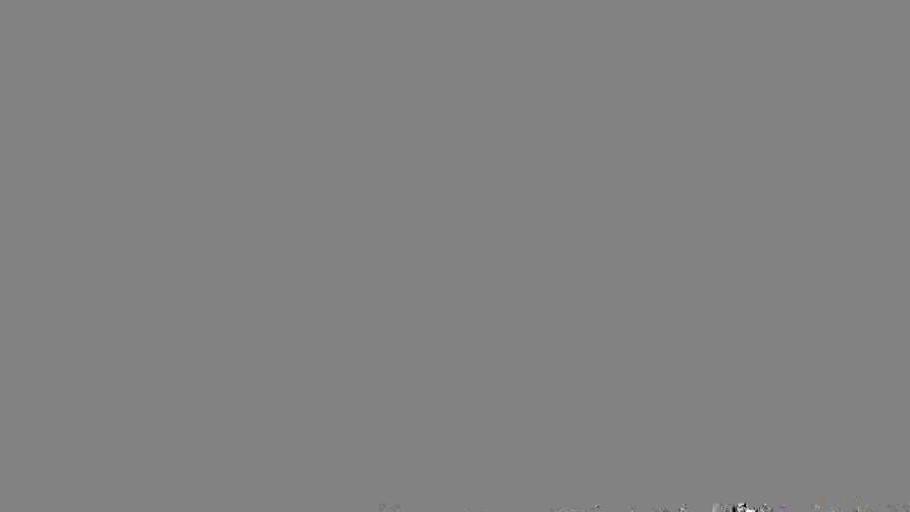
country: TH
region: Buriram
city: Buriram
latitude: 14.9319
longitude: 103.0852
